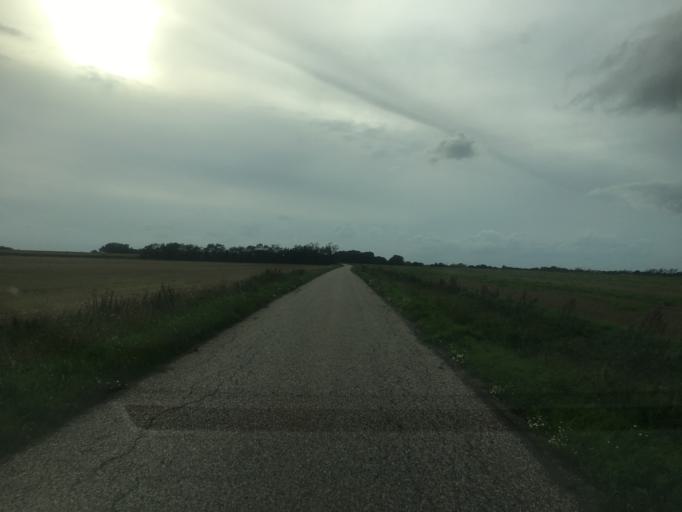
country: DE
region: Schleswig-Holstein
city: Aventoft
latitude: 54.9696
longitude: 8.7606
